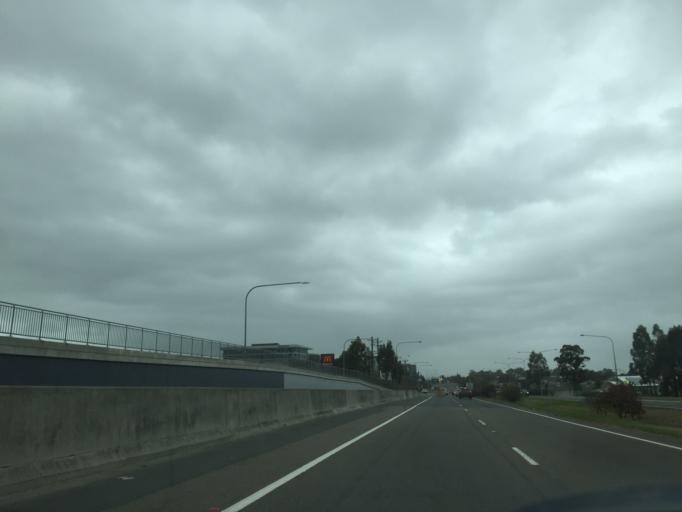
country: AU
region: New South Wales
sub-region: Blacktown
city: Stanhope Gardens
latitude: -33.7304
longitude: 150.9424
